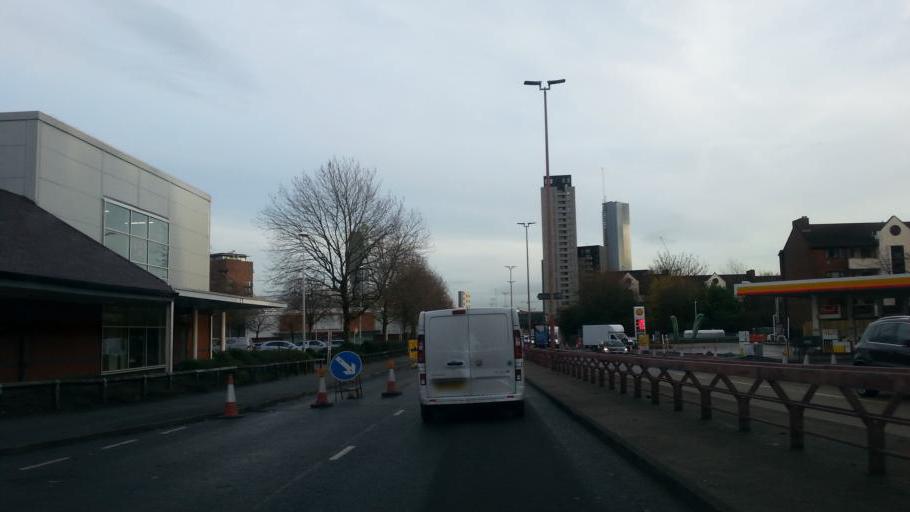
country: GB
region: England
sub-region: Manchester
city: Hulme
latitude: 53.4765
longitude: -2.2682
